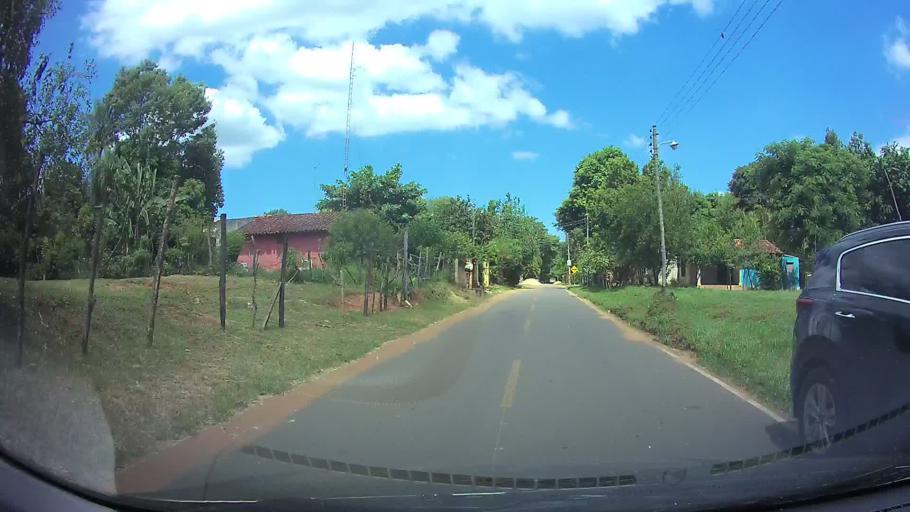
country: PY
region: Central
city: Aregua
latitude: -25.2936
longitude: -57.4204
